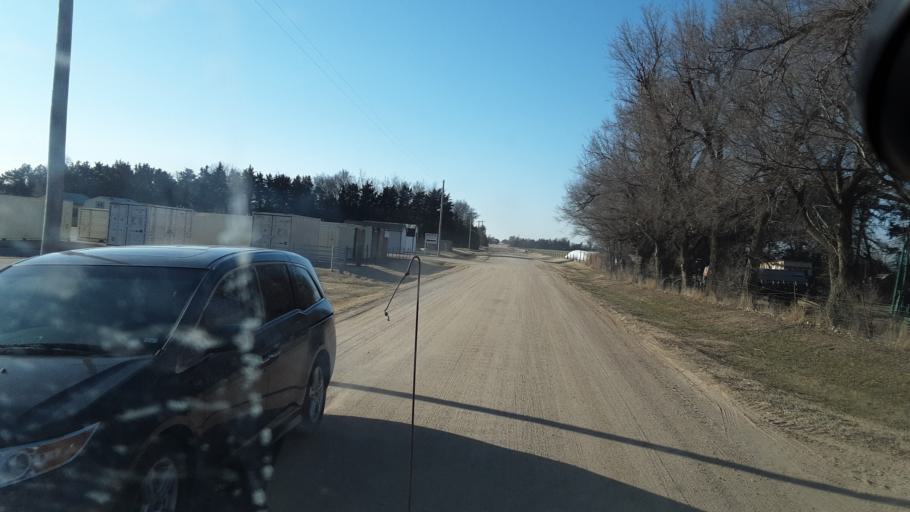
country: US
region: Kansas
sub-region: Reno County
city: South Hutchinson
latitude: 38.0129
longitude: -97.9953
